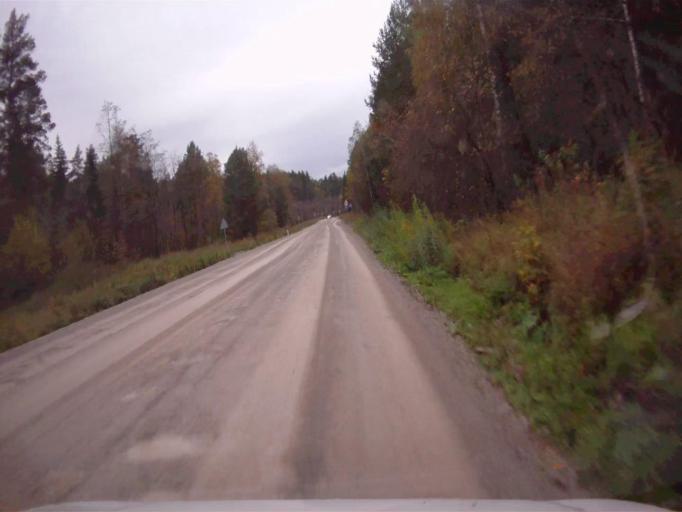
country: RU
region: Chelyabinsk
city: Nyazepetrovsk
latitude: 56.0440
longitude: 59.5057
